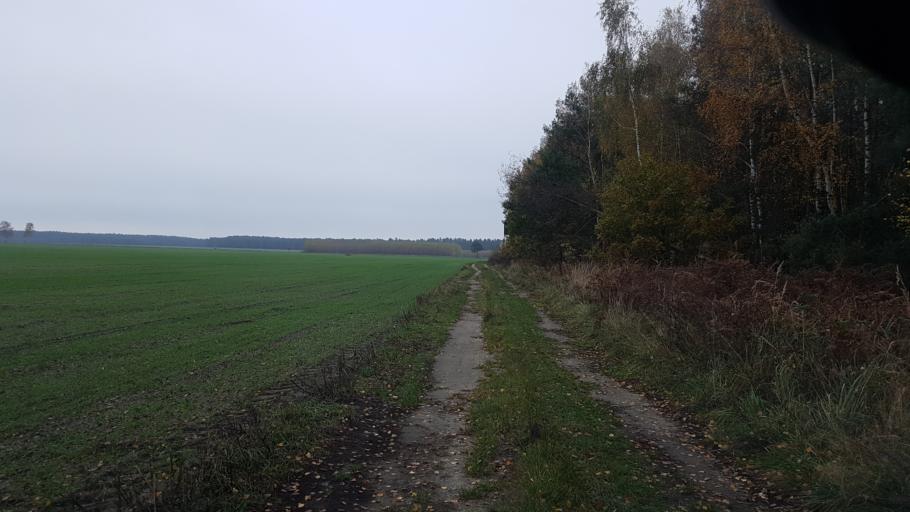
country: DE
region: Brandenburg
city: Ruckersdorf
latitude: 51.5698
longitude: 13.6457
